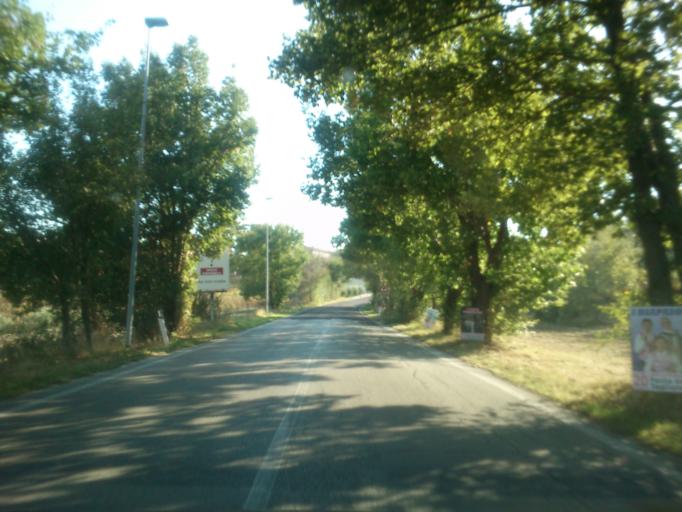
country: IT
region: The Marches
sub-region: Provincia di Pesaro e Urbino
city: Mombaroccio
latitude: 43.8102
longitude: 12.8595
